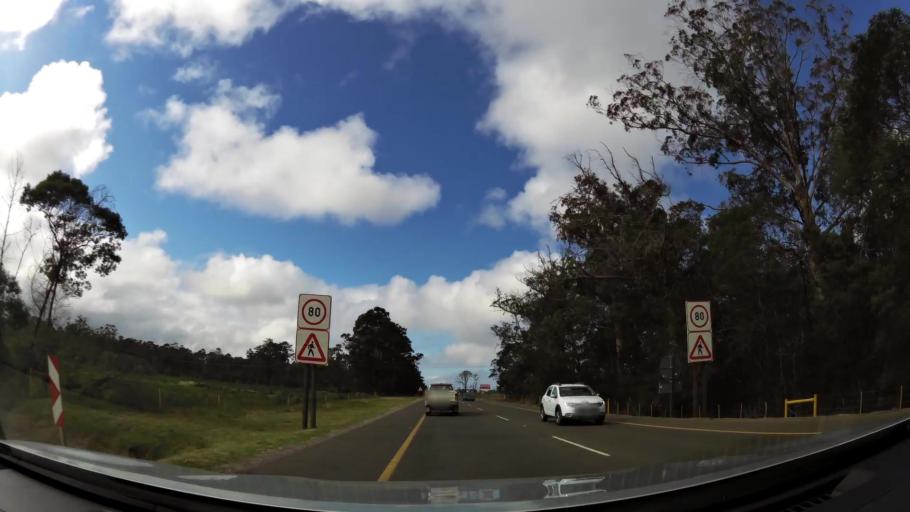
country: ZA
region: Western Cape
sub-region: Eden District Municipality
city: Plettenberg Bay
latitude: -34.0443
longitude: 23.3049
